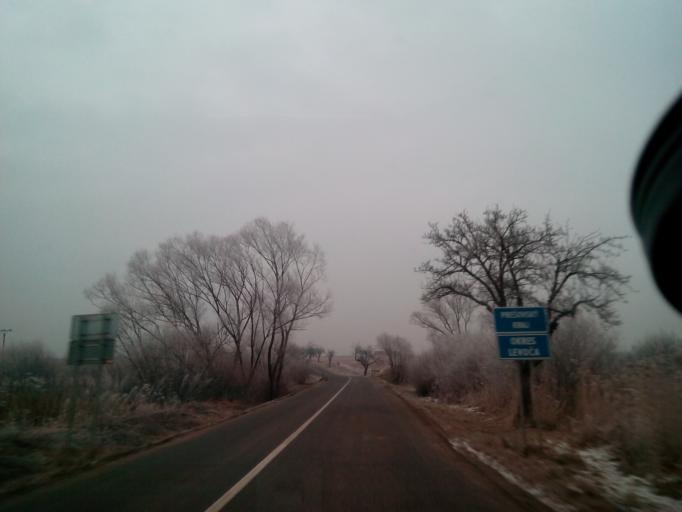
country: SK
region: Presovsky
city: Lubica
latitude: 48.9951
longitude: 20.4481
